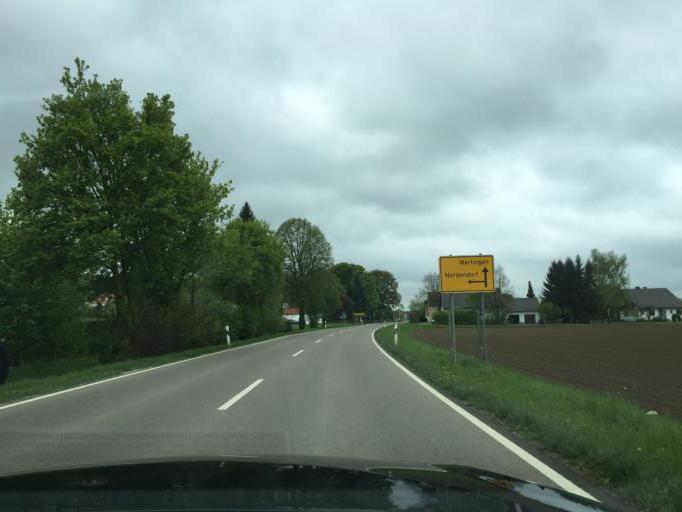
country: DE
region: Bavaria
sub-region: Swabia
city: Buttenwiesen
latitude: 48.5891
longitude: 10.7206
